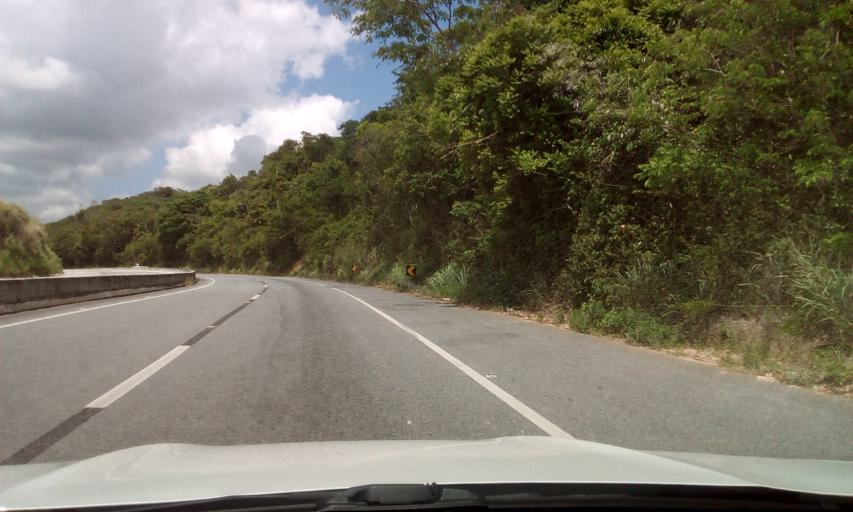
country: BR
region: Alagoas
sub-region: Flexeiras
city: Flexeiras
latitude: -9.2481
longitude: -35.7644
